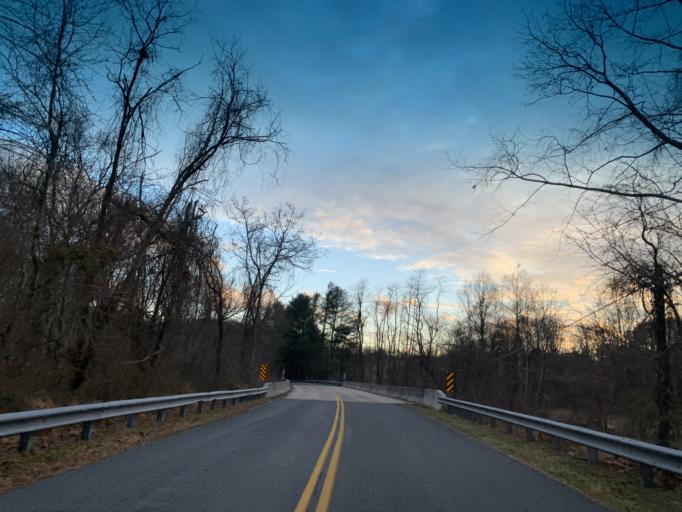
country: US
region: Maryland
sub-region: Harford County
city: Bel Air North
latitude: 39.6264
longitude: -76.3096
